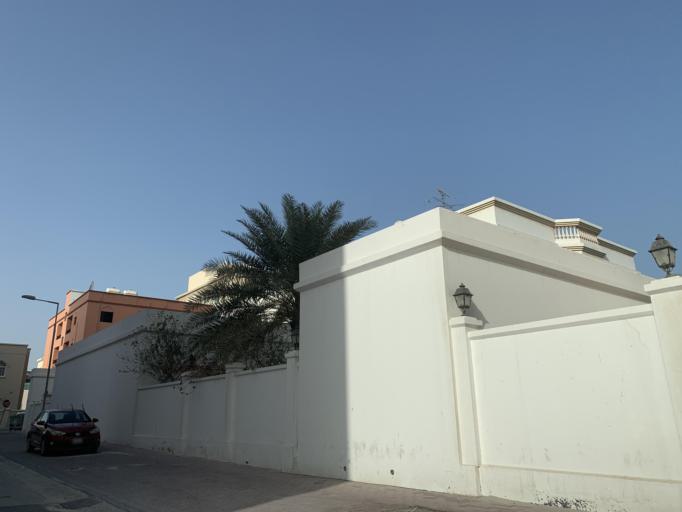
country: BH
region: Manama
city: Manama
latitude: 26.2041
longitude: 50.5846
